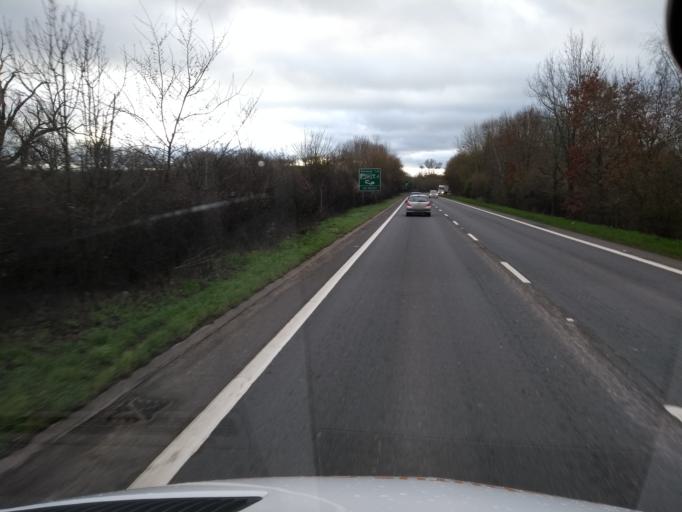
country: GB
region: England
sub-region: Somerset
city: Ilminster
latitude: 50.9362
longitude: -2.9418
